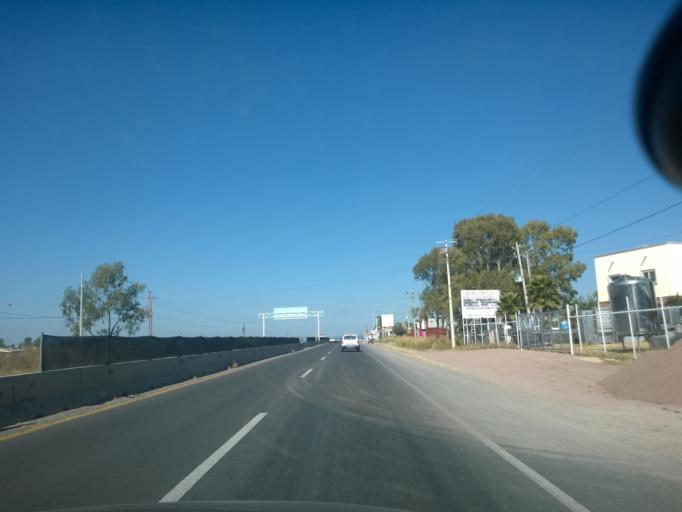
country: MX
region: Guanajuato
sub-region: Leon
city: Fraccionamiento Paseo de las Torres
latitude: 21.2110
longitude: -101.7697
